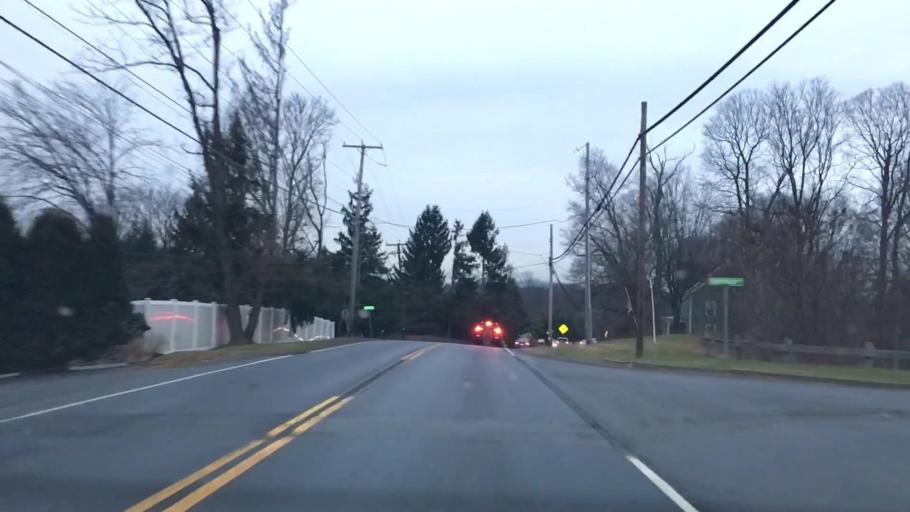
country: US
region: New York
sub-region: Dutchess County
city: Red Oaks Mill
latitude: 41.6540
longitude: -73.8425
